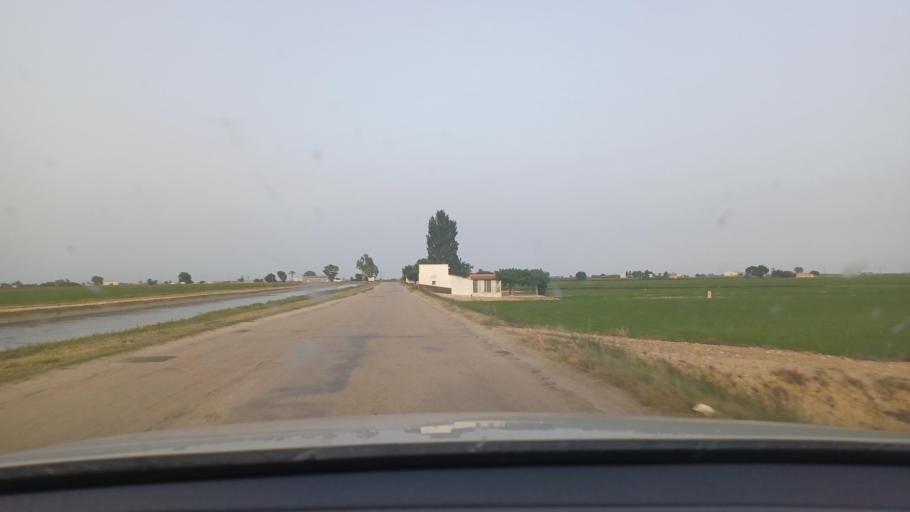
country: ES
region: Catalonia
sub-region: Provincia de Tarragona
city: Amposta
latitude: 40.6998
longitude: 0.6087
